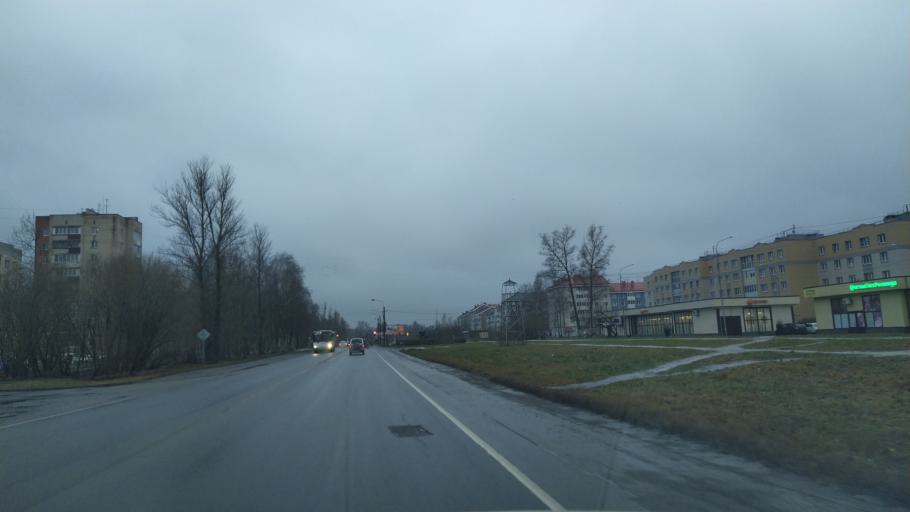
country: RU
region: St.-Petersburg
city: Tyarlevo
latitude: 59.7322
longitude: 30.4677
